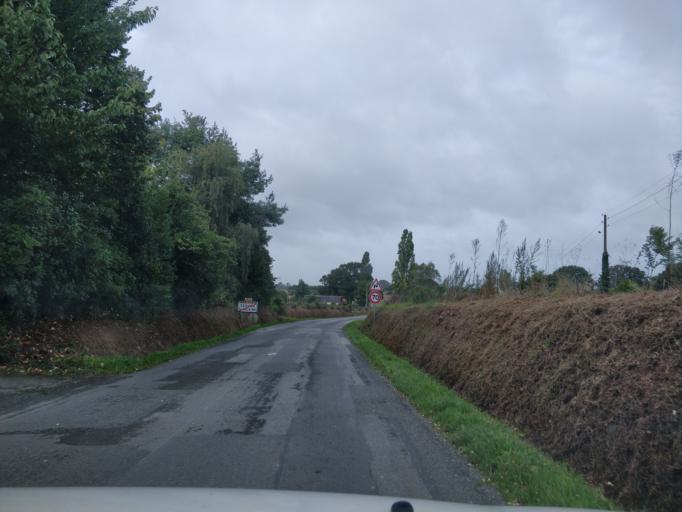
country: FR
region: Brittany
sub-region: Departement d'Ille-et-Vilaine
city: Servon-sur-Vilaine
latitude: 48.1251
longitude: -1.4704
